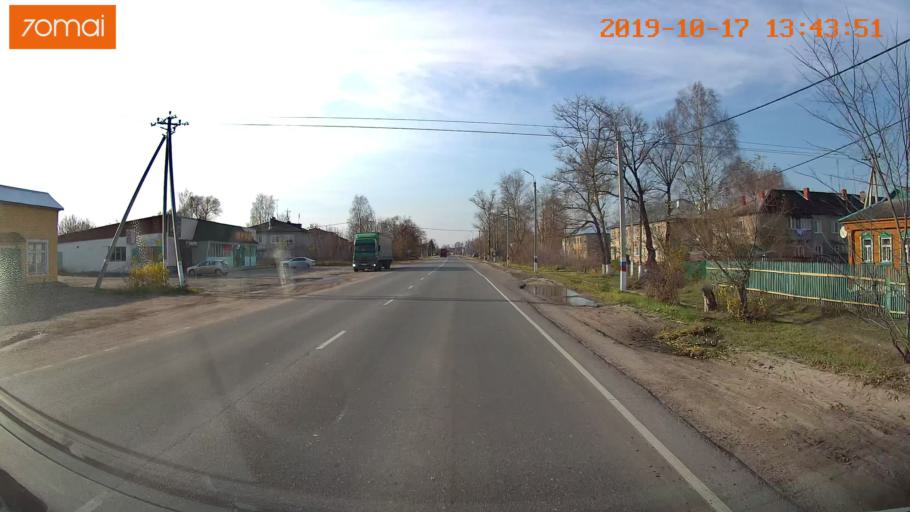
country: RU
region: Rjazan
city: Tuma
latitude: 55.1457
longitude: 40.5372
